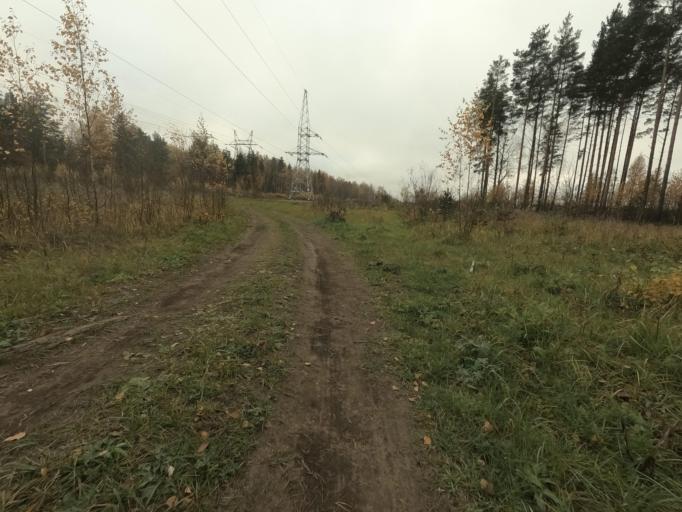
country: RU
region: Leningrad
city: Kirovsk
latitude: 59.8485
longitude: 30.9826
